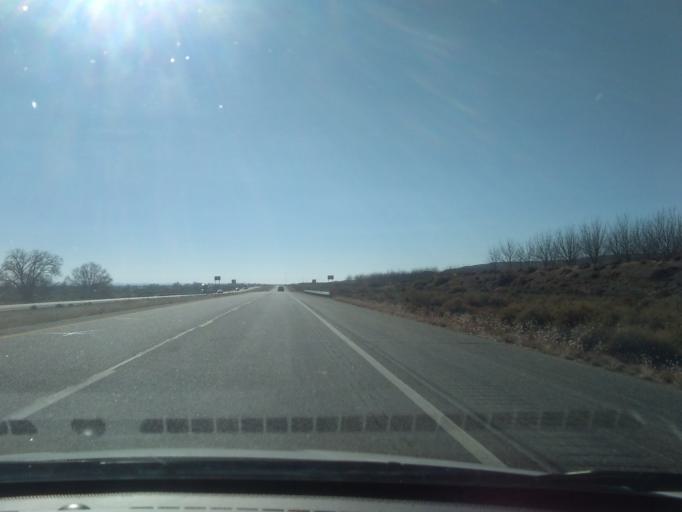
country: US
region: New Mexico
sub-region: Valencia County
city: Jarales
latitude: 34.5755
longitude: -106.7924
